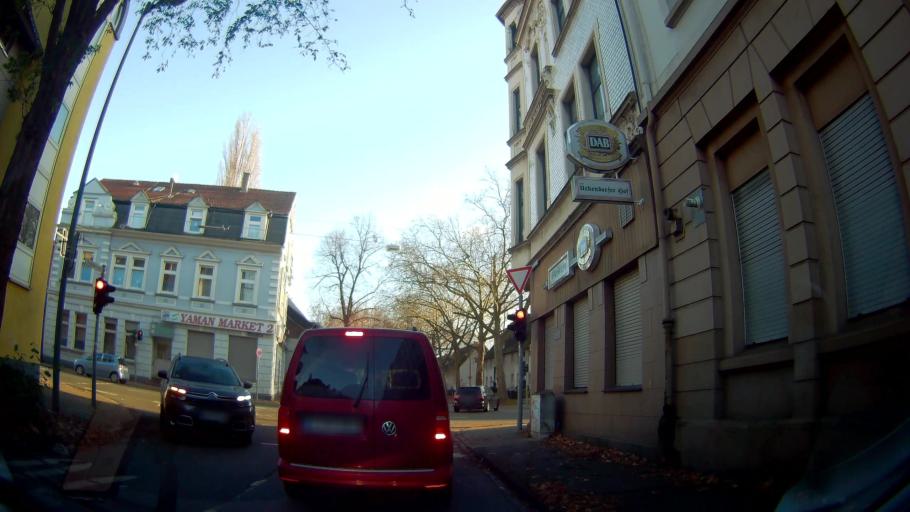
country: DE
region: North Rhine-Westphalia
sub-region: Regierungsbezirk Munster
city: Gelsenkirchen
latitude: 51.5016
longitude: 7.1180
